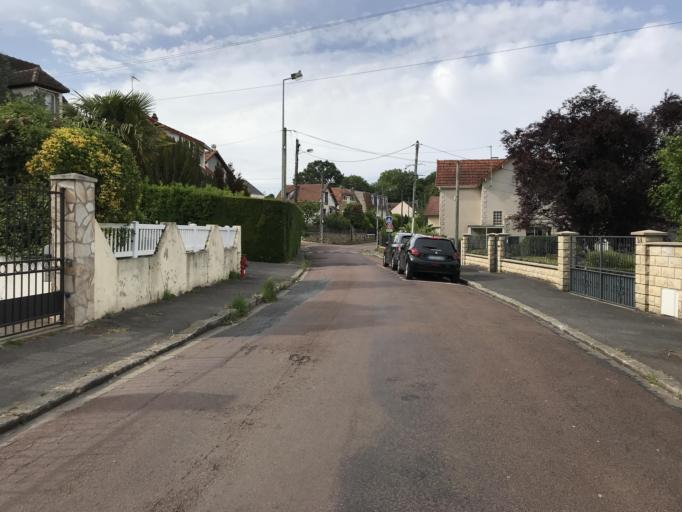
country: FR
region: Ile-de-France
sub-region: Departement de l'Essonne
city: Longpont-sur-Orge
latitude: 48.6327
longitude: 2.2897
